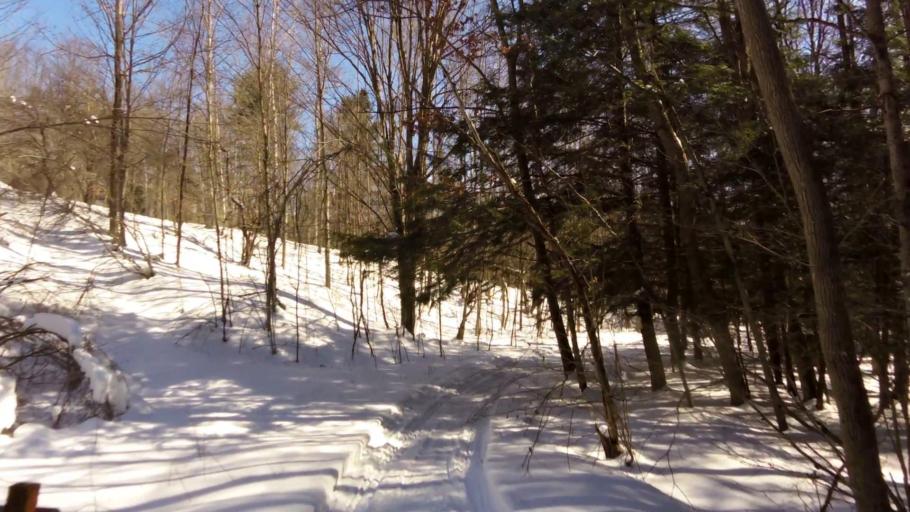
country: US
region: New York
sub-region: Allegany County
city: Cuba
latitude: 42.2824
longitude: -78.2334
